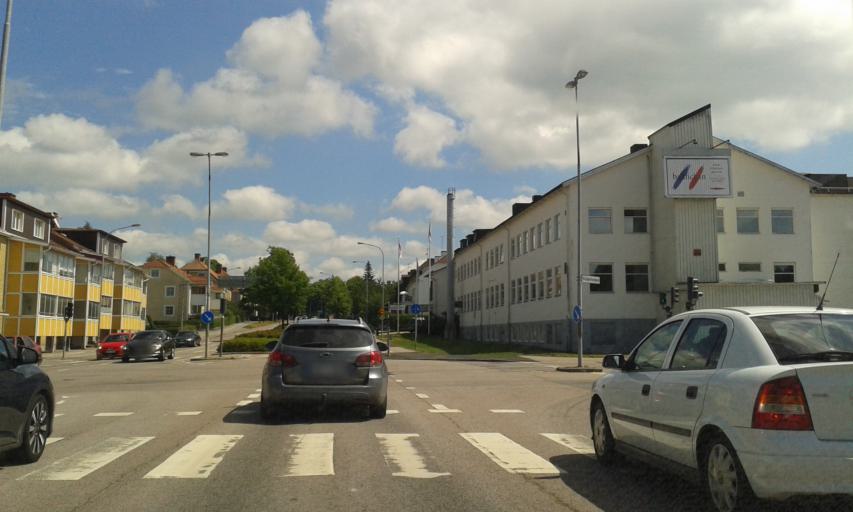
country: SE
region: Kronoberg
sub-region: Vaxjo Kommun
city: Vaexjoe
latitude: 56.8788
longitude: 14.7846
